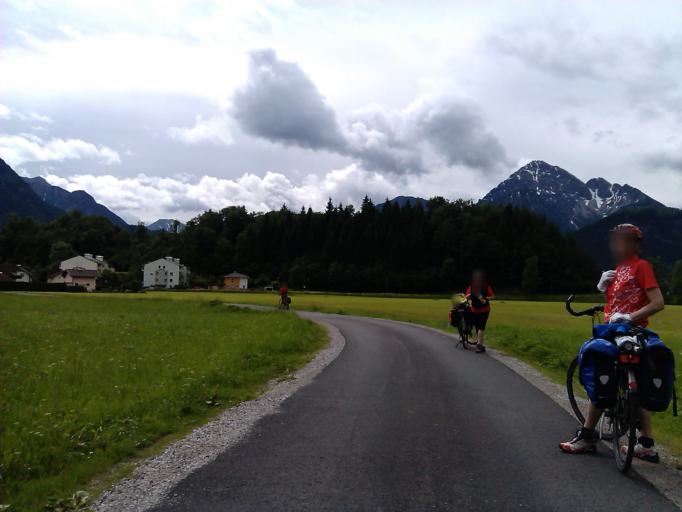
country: AT
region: Tyrol
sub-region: Politischer Bezirk Reutte
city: Lechaschau
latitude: 47.4920
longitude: 10.7114
